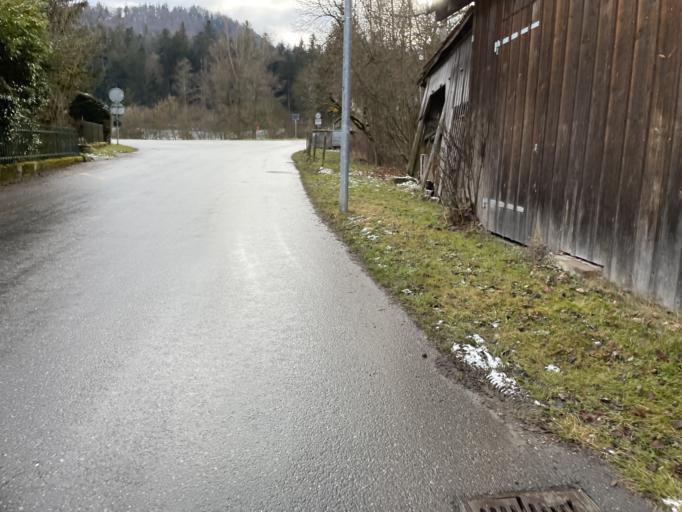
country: CH
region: Bern
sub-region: Thun District
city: Heimberg
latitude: 46.8100
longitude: 7.6129
